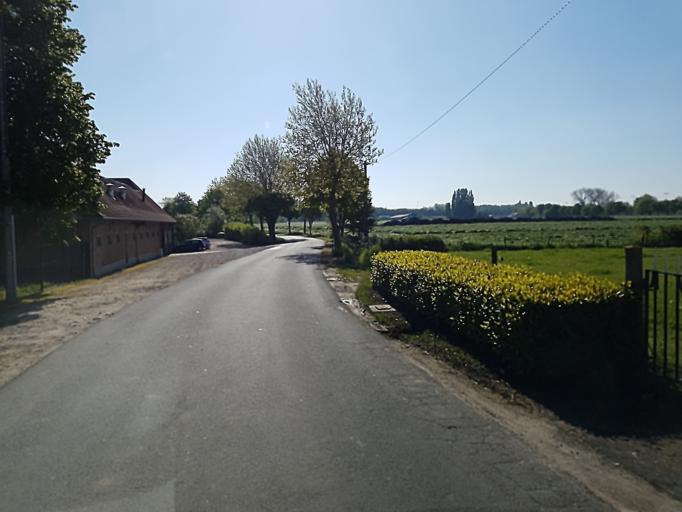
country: BE
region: Wallonia
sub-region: Province du Hainaut
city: Estaimpuis
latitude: 50.7343
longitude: 3.2855
